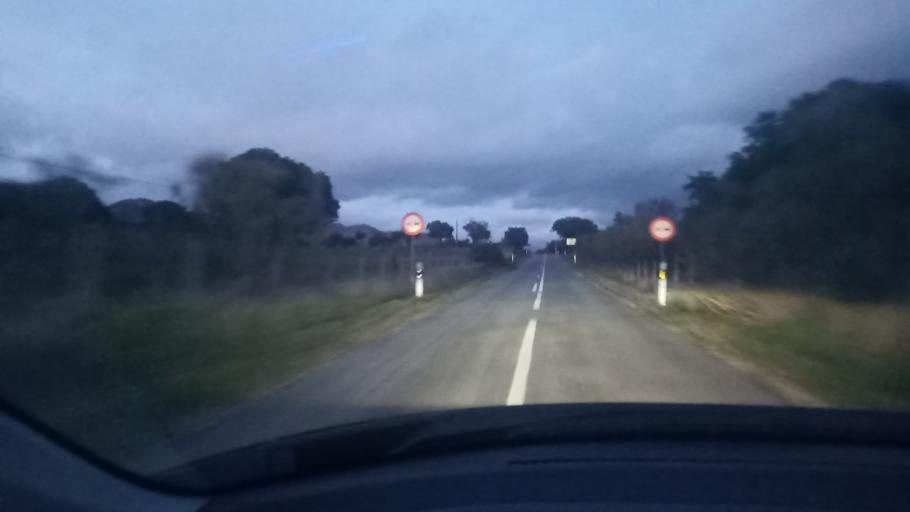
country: ES
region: Madrid
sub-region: Provincia de Madrid
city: Colmenar del Arroyo
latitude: 40.4352
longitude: -4.2446
